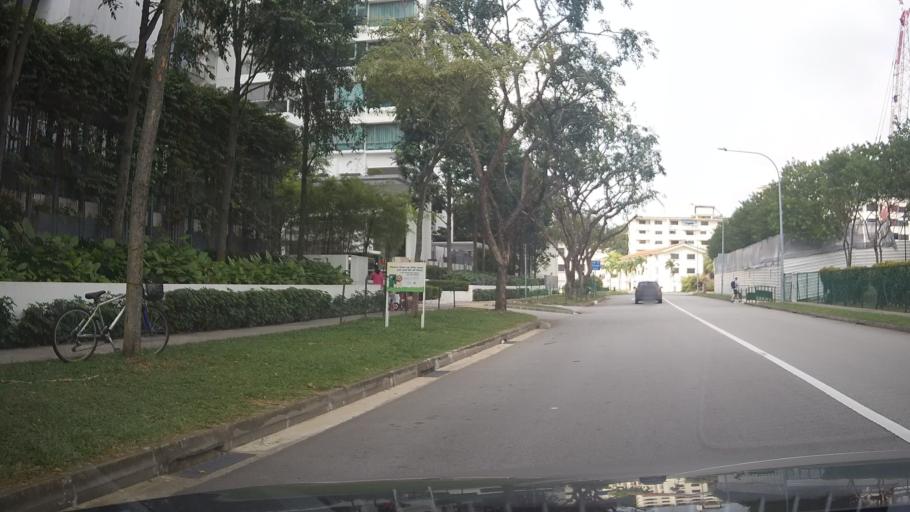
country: SG
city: Singapore
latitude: 1.3067
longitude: 103.8871
